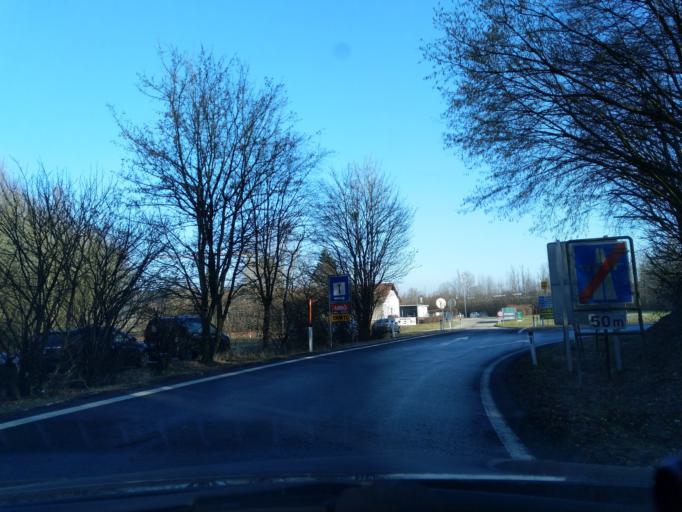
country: AT
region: Upper Austria
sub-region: Politischer Bezirk Ried im Innkreis
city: Ried im Innkreis
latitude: 48.2401
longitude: 13.5089
